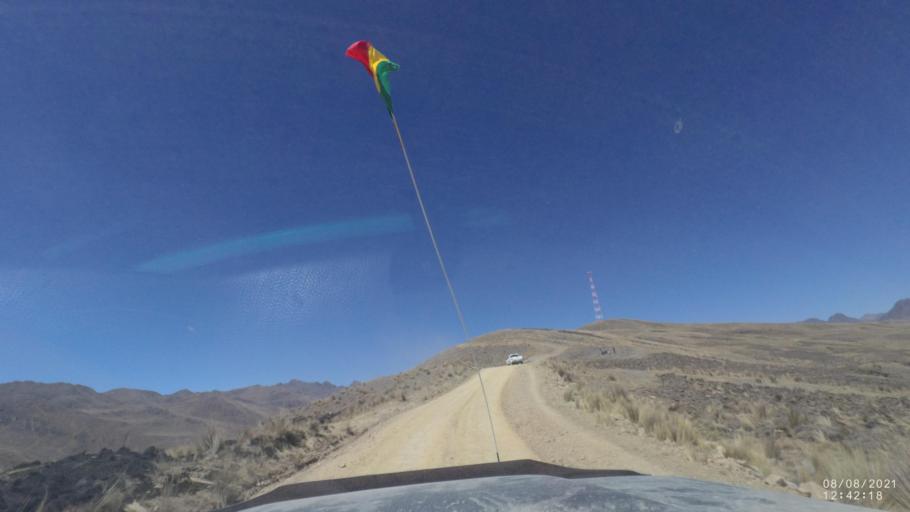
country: BO
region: Cochabamba
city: Colchani
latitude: -16.8390
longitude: -66.6166
